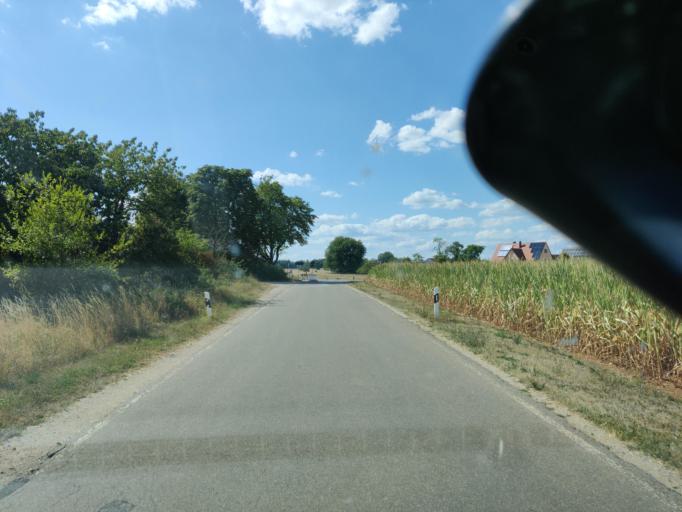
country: DE
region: Bavaria
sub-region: Regierungsbezirk Mittelfranken
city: Thalmassing
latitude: 49.0661
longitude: 11.2272
